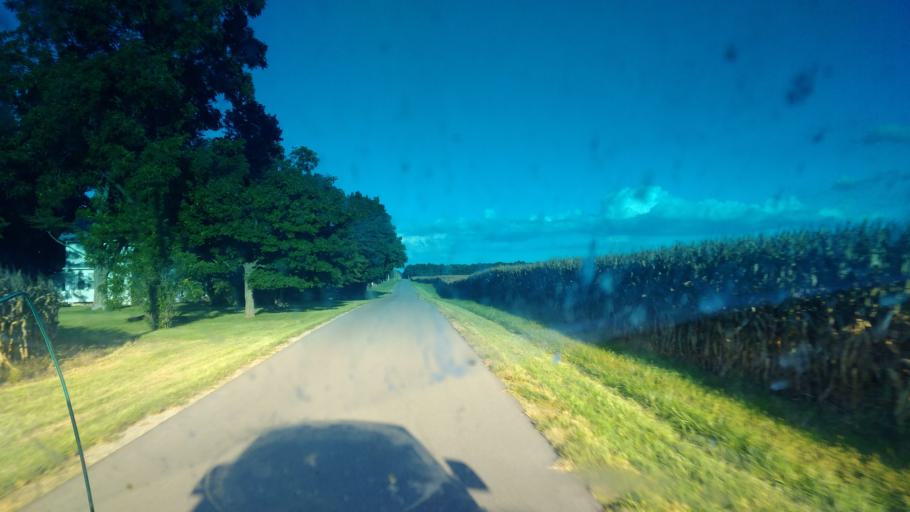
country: US
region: Ohio
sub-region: Wyandot County
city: Upper Sandusky
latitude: 40.8909
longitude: -83.2661
